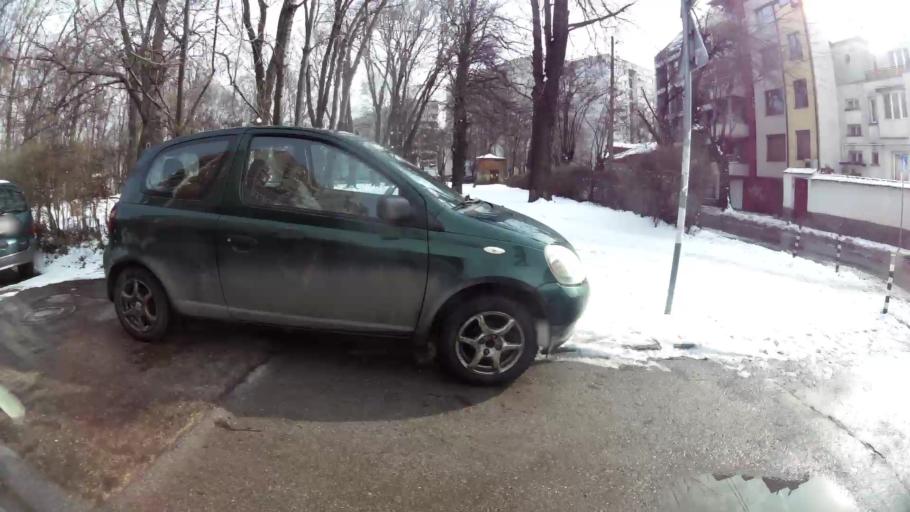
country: BG
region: Sofia-Capital
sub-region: Stolichna Obshtina
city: Sofia
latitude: 42.7065
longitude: 23.3435
